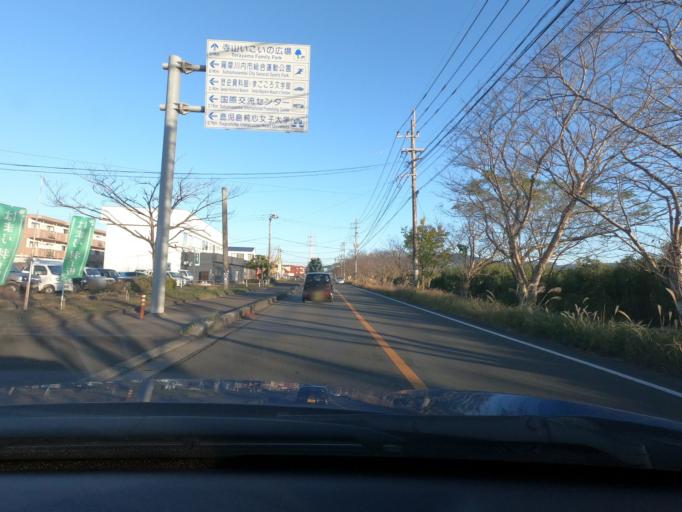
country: JP
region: Kagoshima
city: Satsumasendai
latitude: 31.8096
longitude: 130.3178
